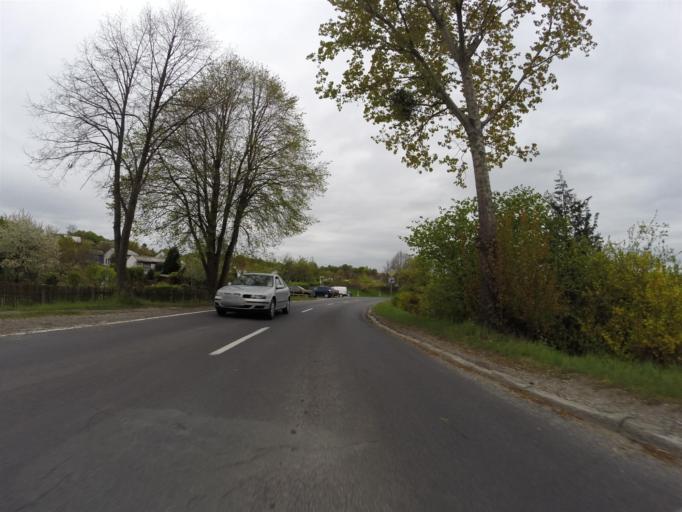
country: DE
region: Saxony-Anhalt
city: Naumburg
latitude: 51.1454
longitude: 11.7976
